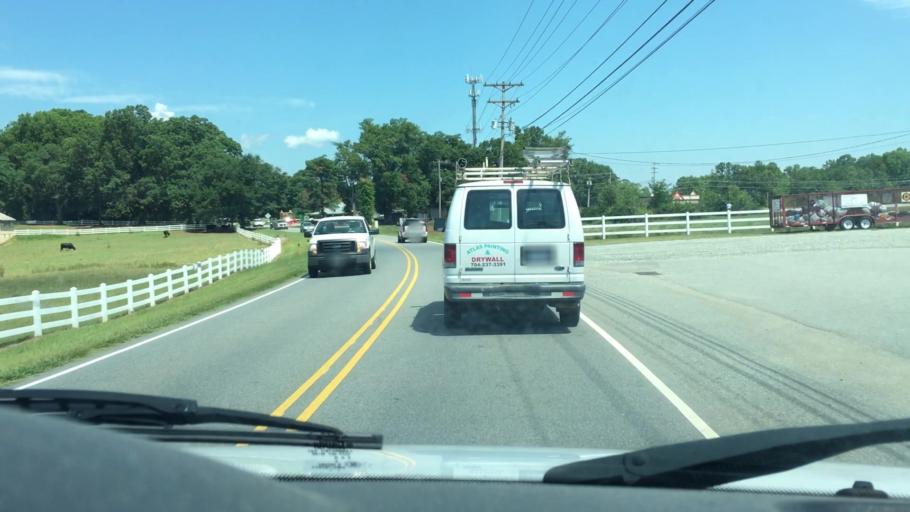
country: US
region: North Carolina
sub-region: Mecklenburg County
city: Huntersville
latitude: 35.4237
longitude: -80.9157
